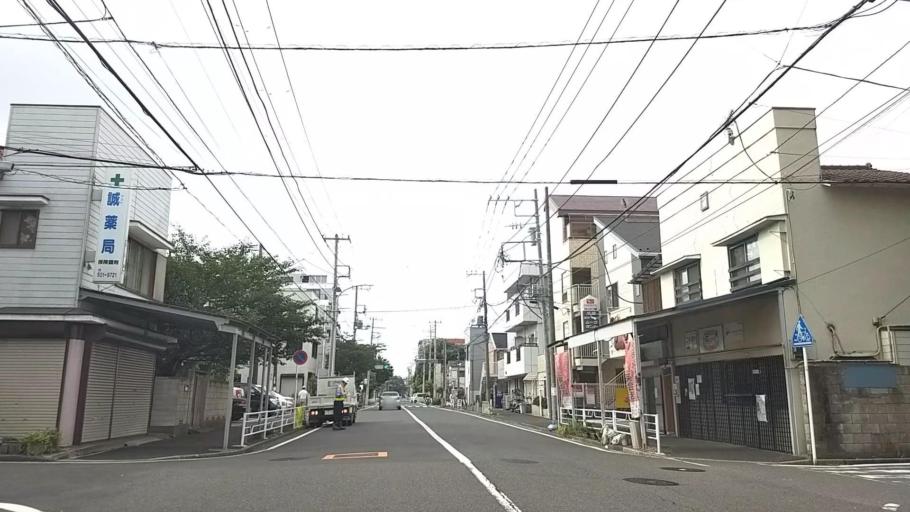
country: JP
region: Kanagawa
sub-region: Kawasaki-shi
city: Kawasaki
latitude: 35.5079
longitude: 139.6890
